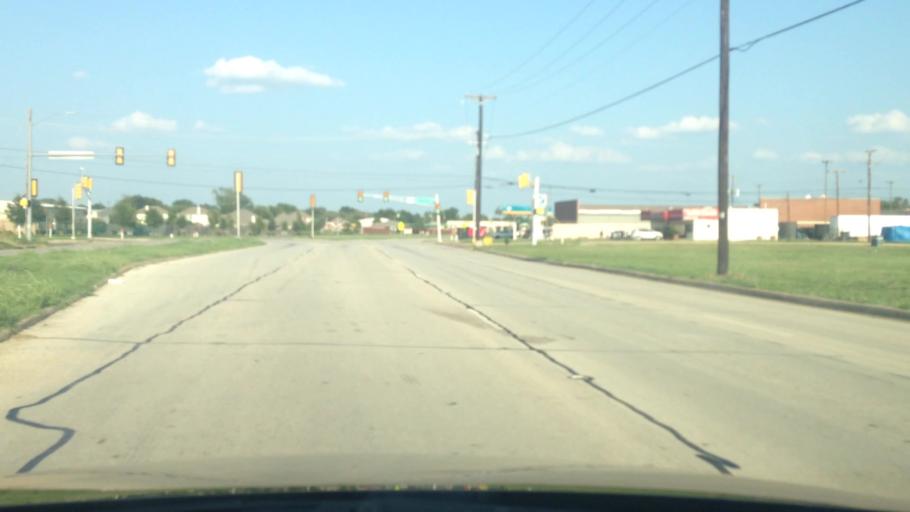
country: US
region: Texas
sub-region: Tarrant County
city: Everman
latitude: 32.6274
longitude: -97.3053
